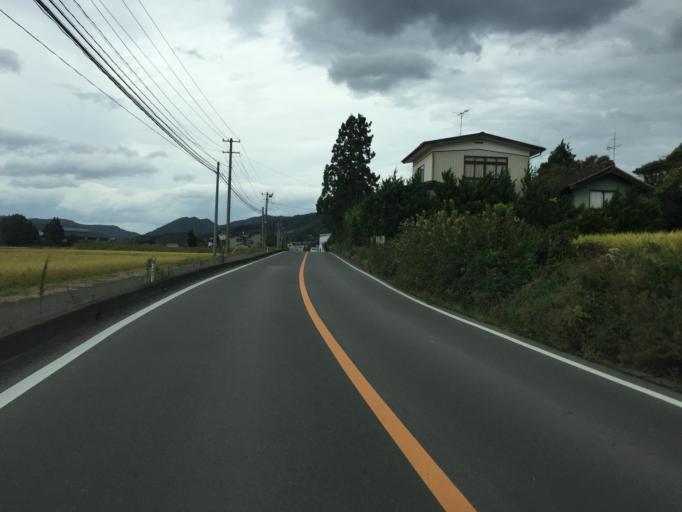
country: JP
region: Fukushima
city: Yanagawamachi-saiwaicho
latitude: 37.8685
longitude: 140.6235
